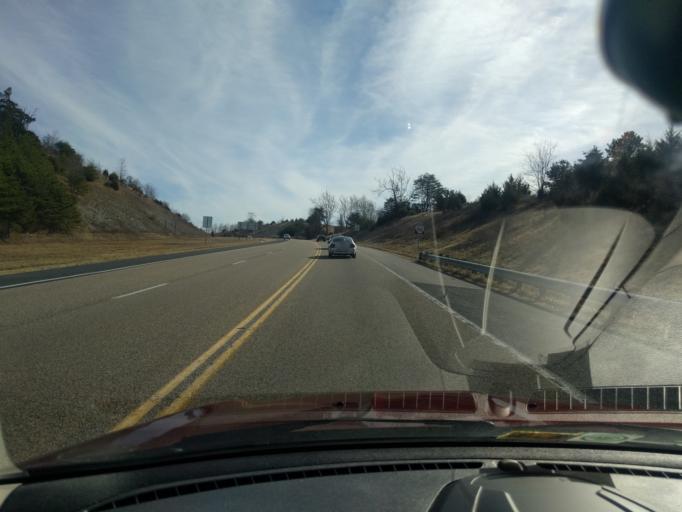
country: US
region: Virginia
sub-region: Augusta County
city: Jolivue
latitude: 38.1285
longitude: -79.0901
